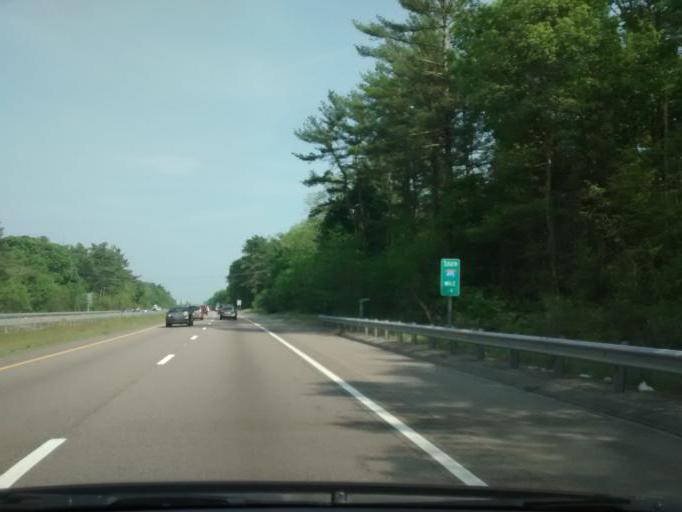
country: US
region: Massachusetts
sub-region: Plymouth County
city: Middleborough Center
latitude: 41.8959
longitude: -70.9541
